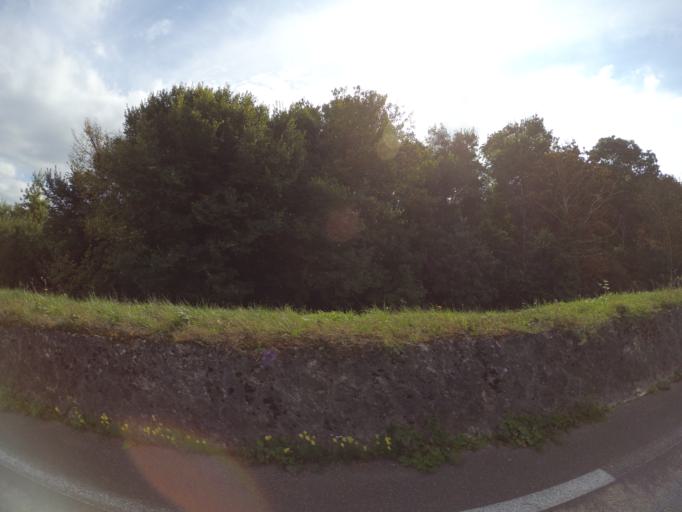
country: FR
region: Centre
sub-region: Departement d'Indre-et-Loire
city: Vouvray
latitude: 47.4101
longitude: 0.7922
